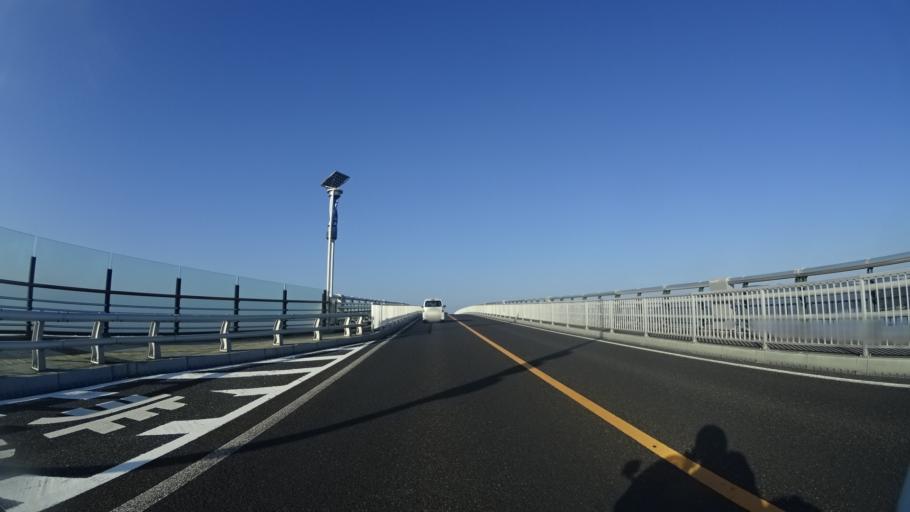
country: JP
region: Shimane
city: Sakaiminato
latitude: 35.5198
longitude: 133.2015
